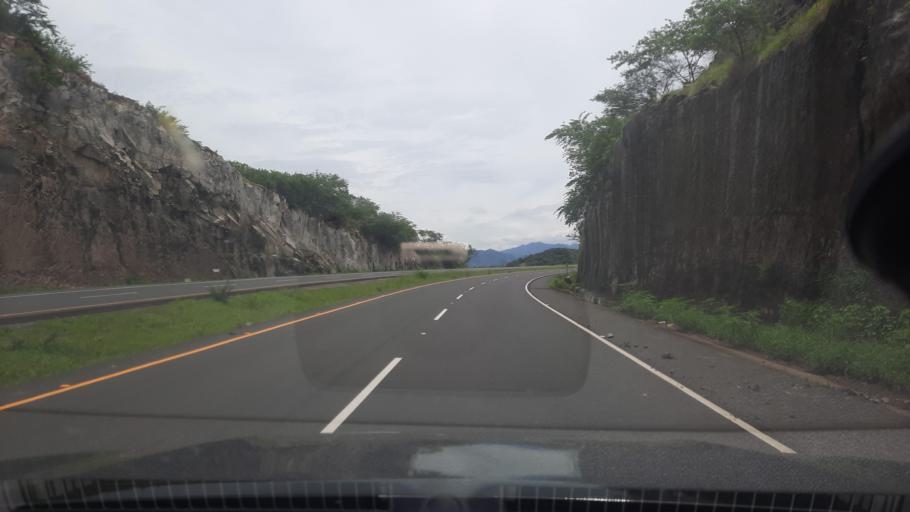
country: HN
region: Valle
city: Aramecina
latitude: 13.7357
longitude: -87.7198
